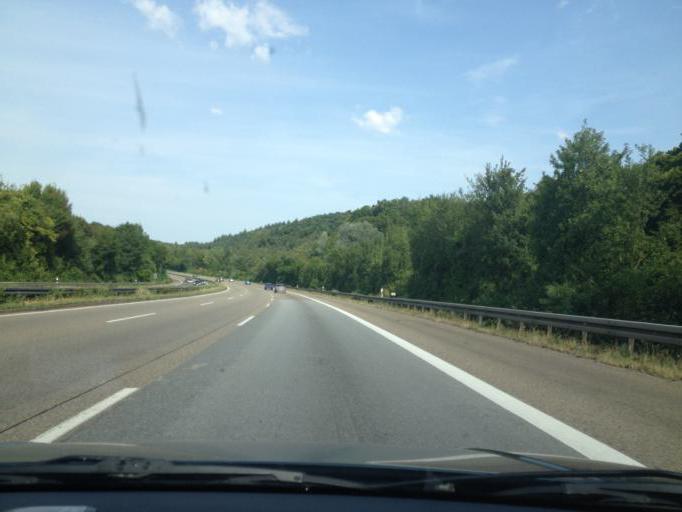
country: DE
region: Baden-Wuerttemberg
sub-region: Karlsruhe Region
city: Dielheim
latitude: 49.2749
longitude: 8.7421
